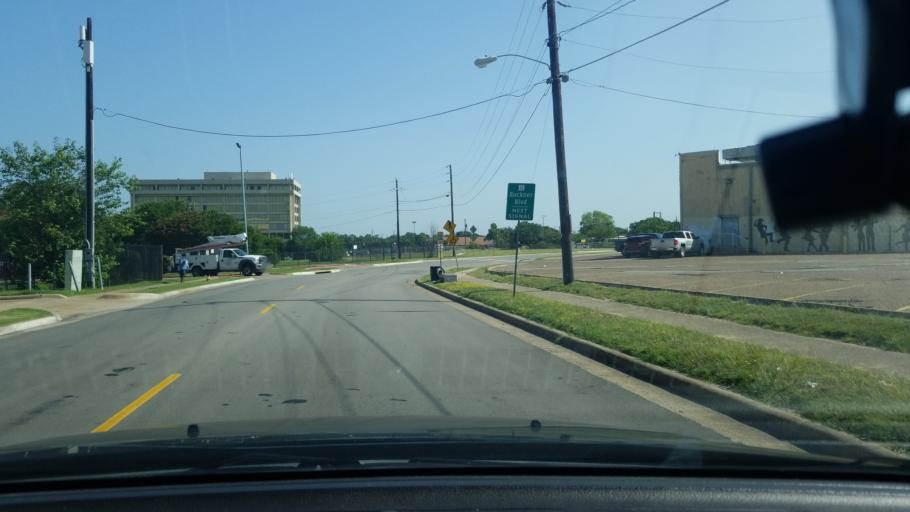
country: US
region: Texas
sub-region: Dallas County
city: Mesquite
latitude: 32.8074
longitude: -96.6855
